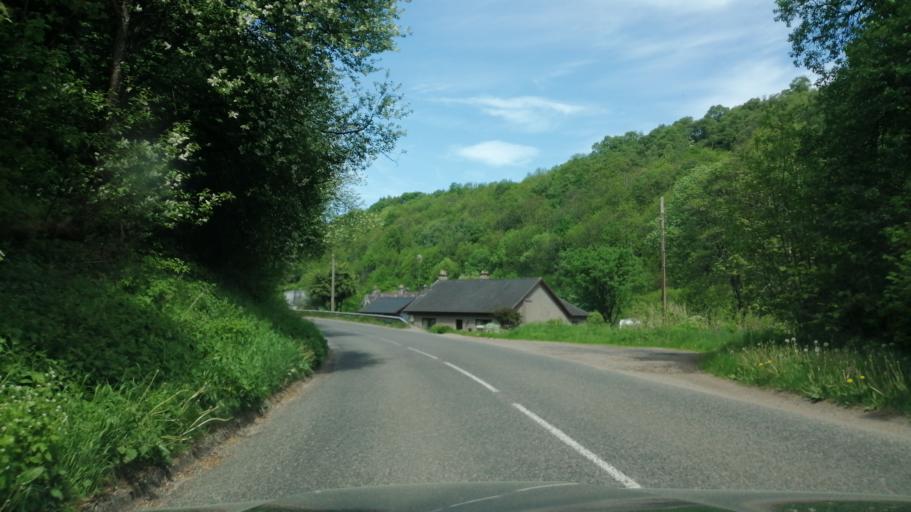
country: GB
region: Scotland
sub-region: Moray
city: Dufftown
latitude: 57.4460
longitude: -3.1168
